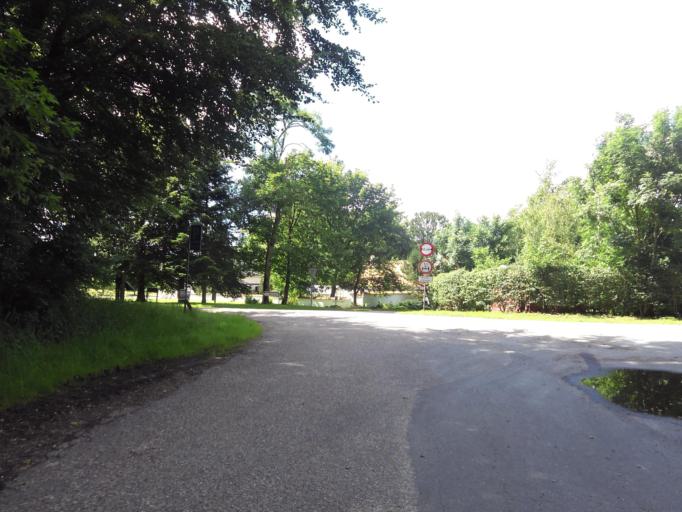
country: DK
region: South Denmark
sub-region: Haderslev Kommune
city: Vojens
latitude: 55.3151
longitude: 9.1970
